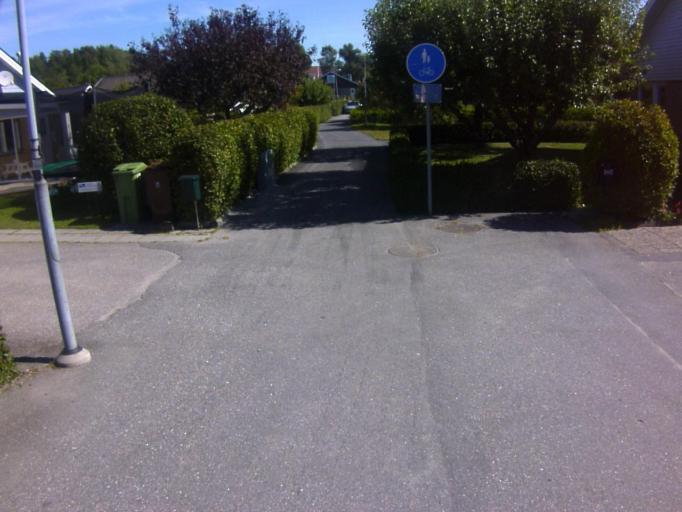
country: SE
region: Soedermanland
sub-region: Strangnas Kommun
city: Strangnas
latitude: 59.4166
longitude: 16.9310
